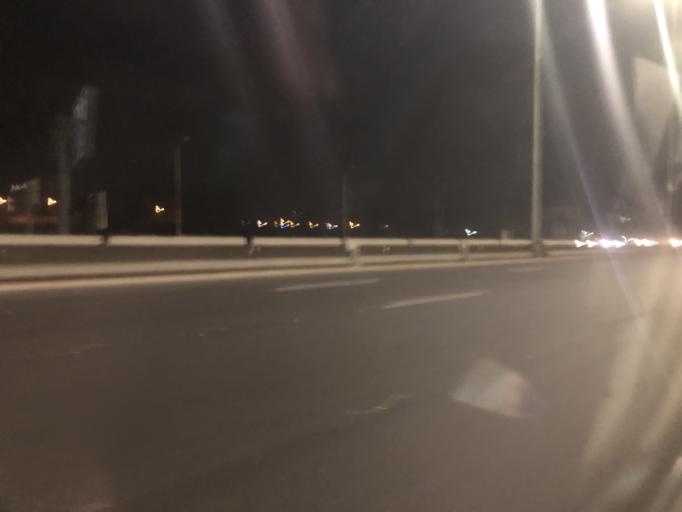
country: EG
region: Al Jizah
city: Al Jizah
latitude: 29.9801
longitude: 31.1171
